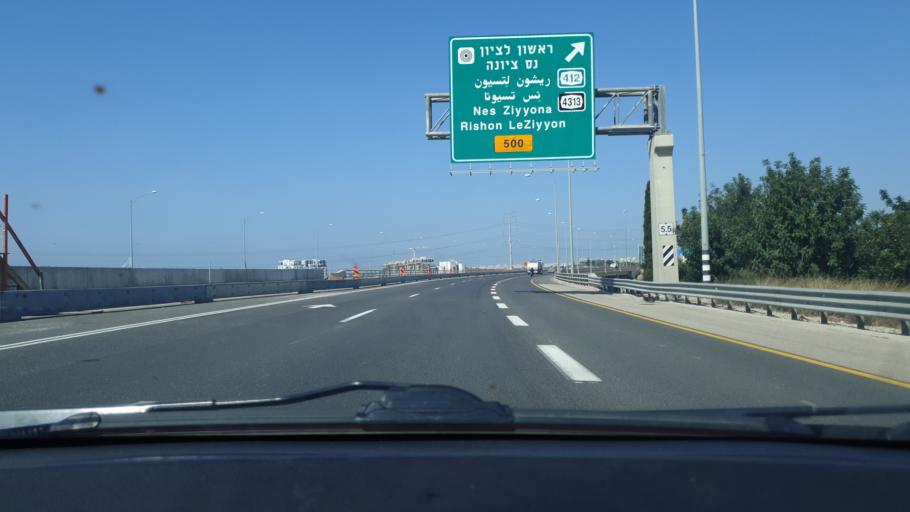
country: IL
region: Central District
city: Ness Ziona
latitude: 31.9326
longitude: 34.8207
